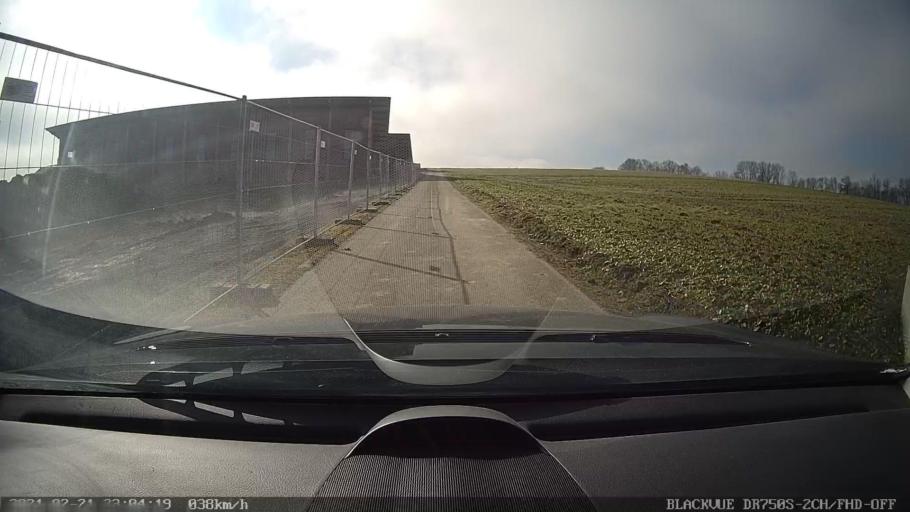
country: DE
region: Bavaria
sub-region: Upper Bavaria
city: Griesstatt
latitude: 48.0020
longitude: 12.1776
